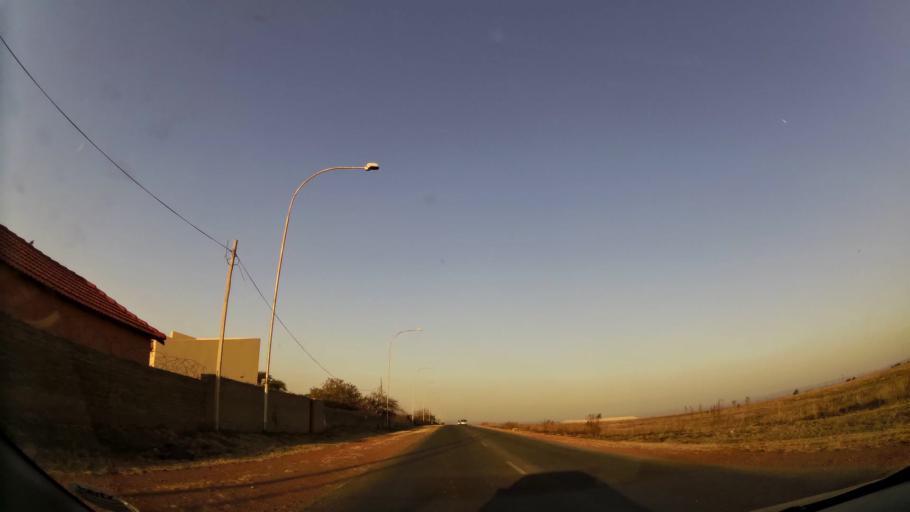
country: ZA
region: Gauteng
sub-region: West Rand District Municipality
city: Randfontein
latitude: -26.2097
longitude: 27.7004
